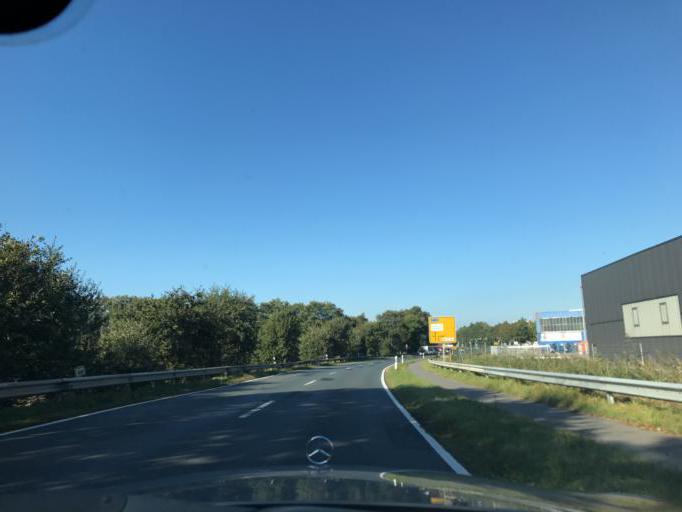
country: DE
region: Lower Saxony
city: Papenburg
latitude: 53.0848
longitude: 7.3747
